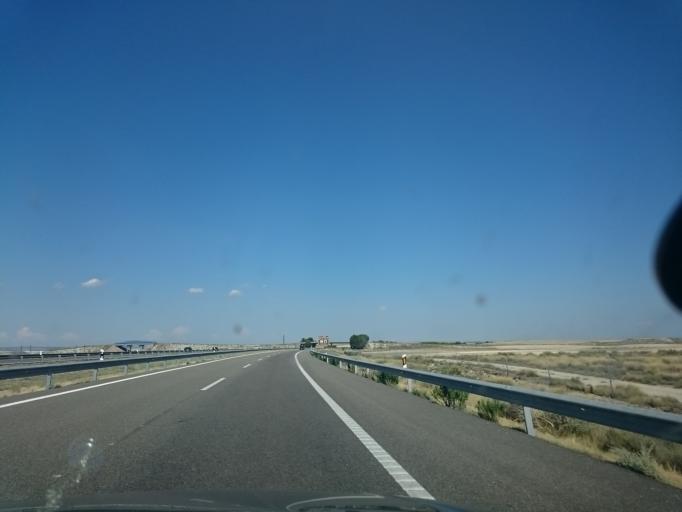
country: ES
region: Aragon
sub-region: Provincia de Zaragoza
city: Bujaraloz
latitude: 41.5247
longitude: -0.2016
